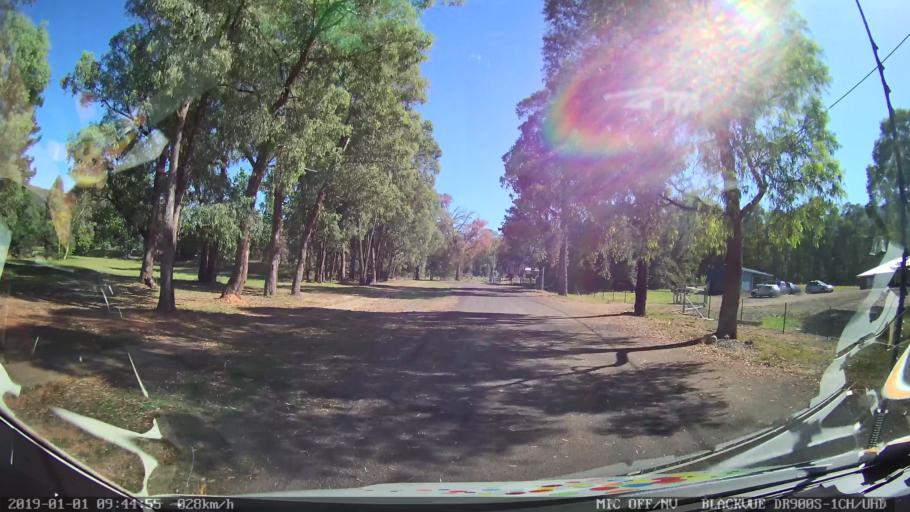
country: AU
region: New South Wales
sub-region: Snowy River
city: Jindabyne
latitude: -36.2115
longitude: 148.1369
